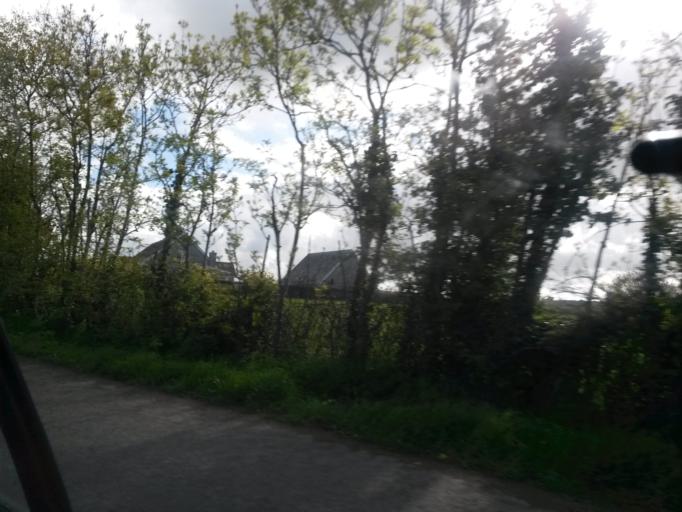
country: IE
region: Leinster
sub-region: Loch Garman
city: Ferns
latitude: 52.5741
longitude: -6.5173
